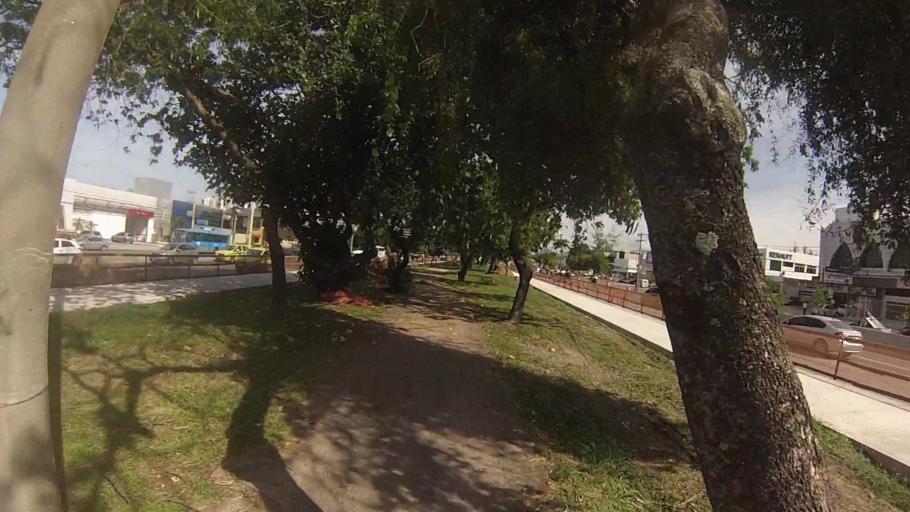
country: BR
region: Rio de Janeiro
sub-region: Rio De Janeiro
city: Rio de Janeiro
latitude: -23.0007
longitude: -43.3330
